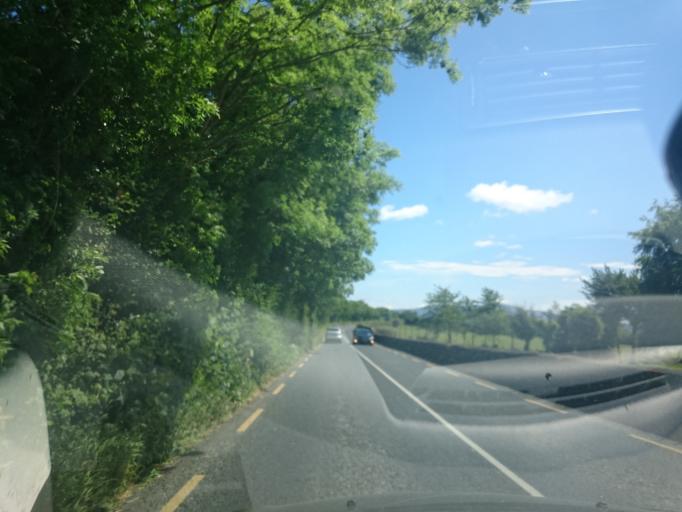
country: IE
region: Leinster
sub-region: County Carlow
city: Bagenalstown
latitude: 52.6319
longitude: -7.0578
